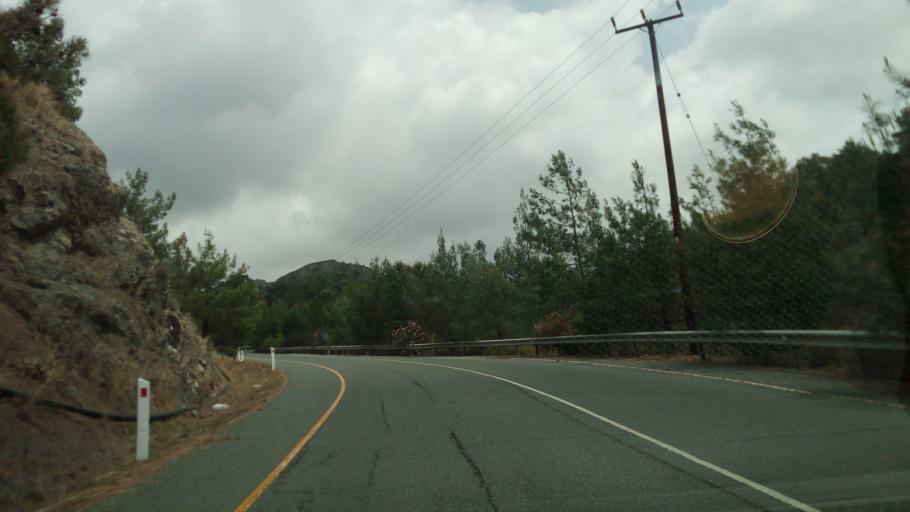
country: CY
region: Limassol
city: Pelendri
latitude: 34.8651
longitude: 32.9216
